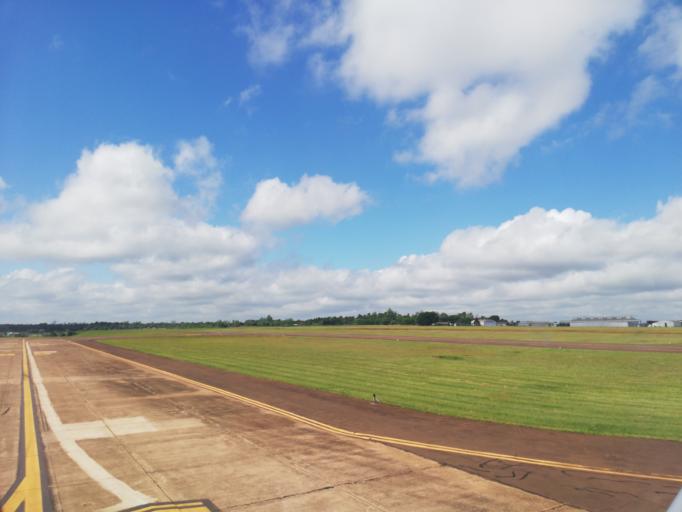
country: AR
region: Misiones
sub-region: Departamento de Capital
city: Posadas
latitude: -27.3910
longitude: -55.9678
